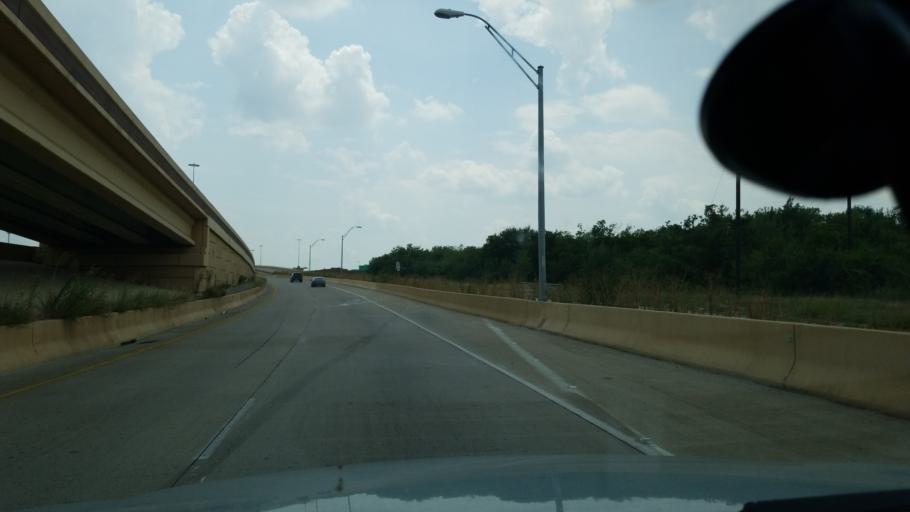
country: US
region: Texas
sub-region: Dallas County
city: Irving
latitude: 32.8443
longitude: -96.9139
